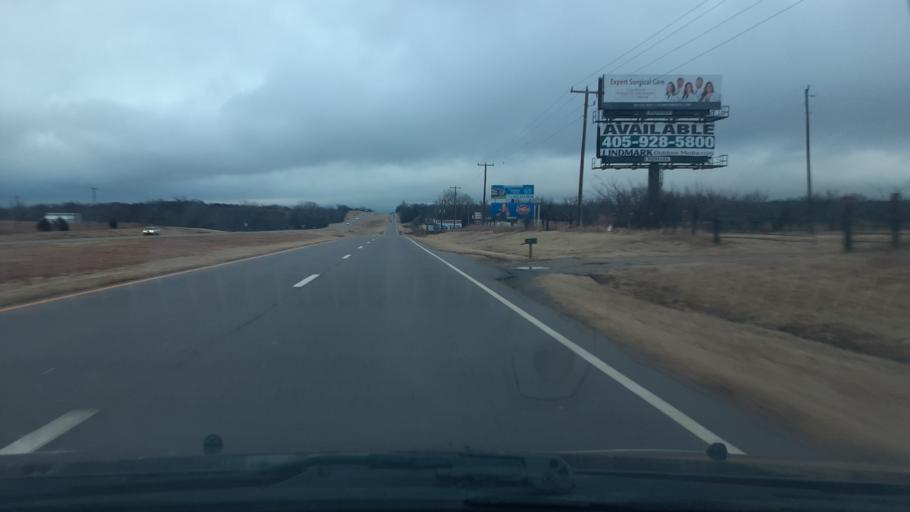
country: US
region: Oklahoma
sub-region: Payne County
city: Stillwater
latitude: 36.1158
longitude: -97.1610
